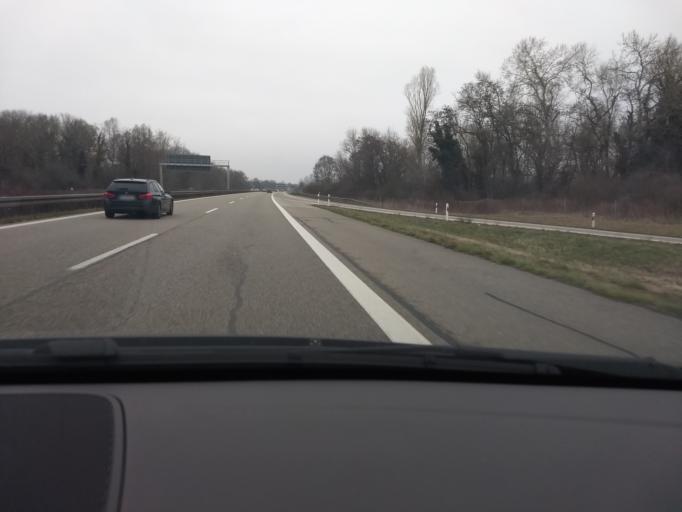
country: FR
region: Alsace
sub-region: Departement du Haut-Rhin
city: Ottmarsheim
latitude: 47.7832
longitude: 7.5364
